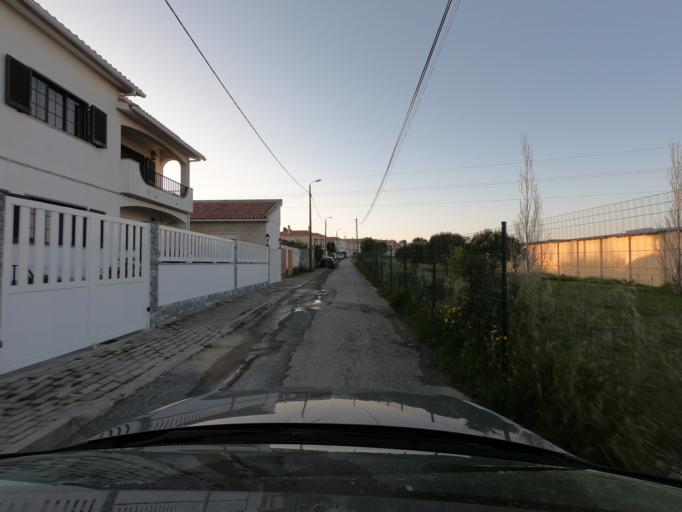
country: PT
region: Lisbon
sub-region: Sintra
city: Rio de Mouro
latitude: 38.7533
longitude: -9.3538
